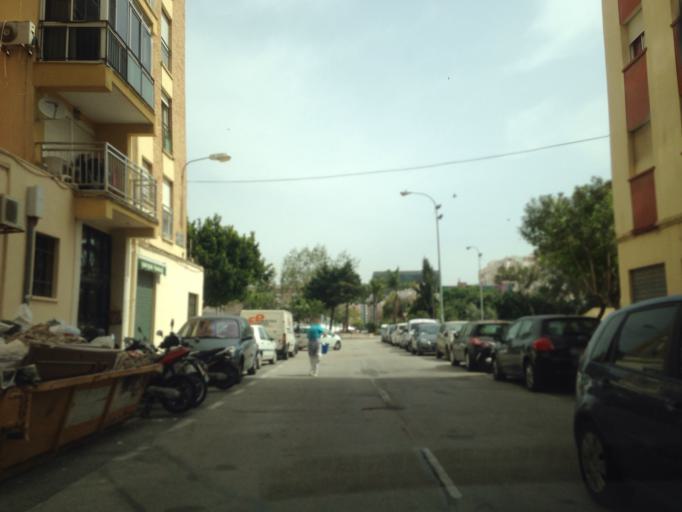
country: ES
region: Andalusia
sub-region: Provincia de Malaga
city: Malaga
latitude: 36.7074
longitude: -4.4314
